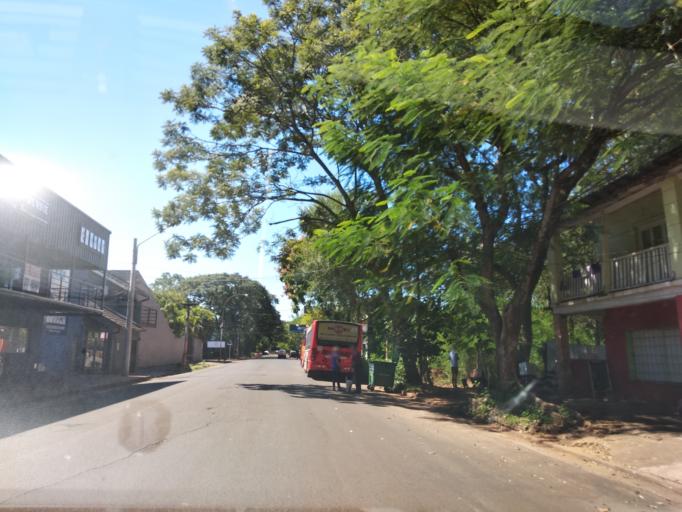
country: AR
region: Misiones
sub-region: Departamento de Iguazu
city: Puerto Iguazu
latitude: -25.5961
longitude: -54.5739
